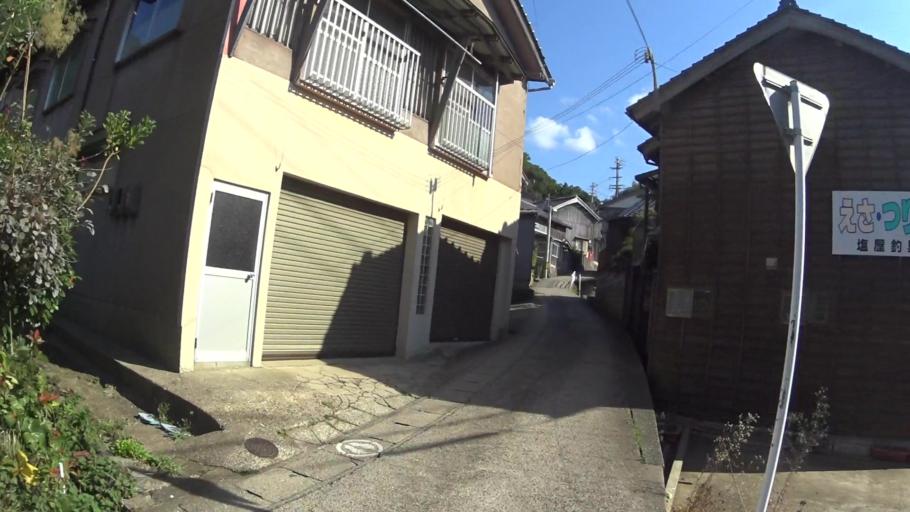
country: JP
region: Kyoto
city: Miyazu
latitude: 35.7374
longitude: 135.0948
